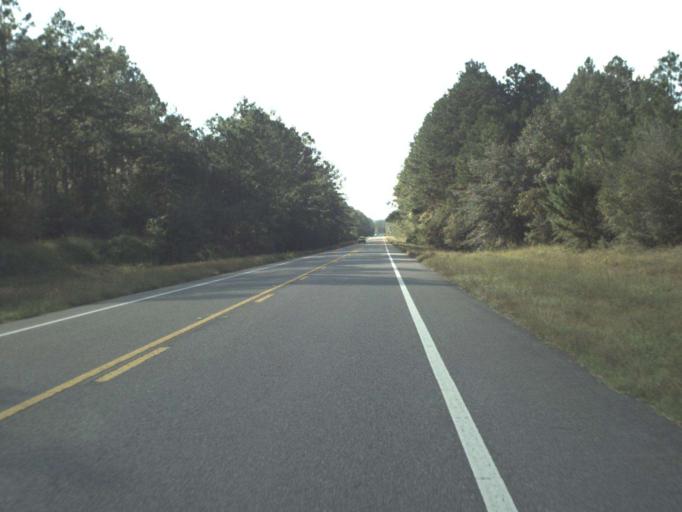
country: US
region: Florida
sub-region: Bay County
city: Laguna Beach
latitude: 30.4423
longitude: -85.8221
